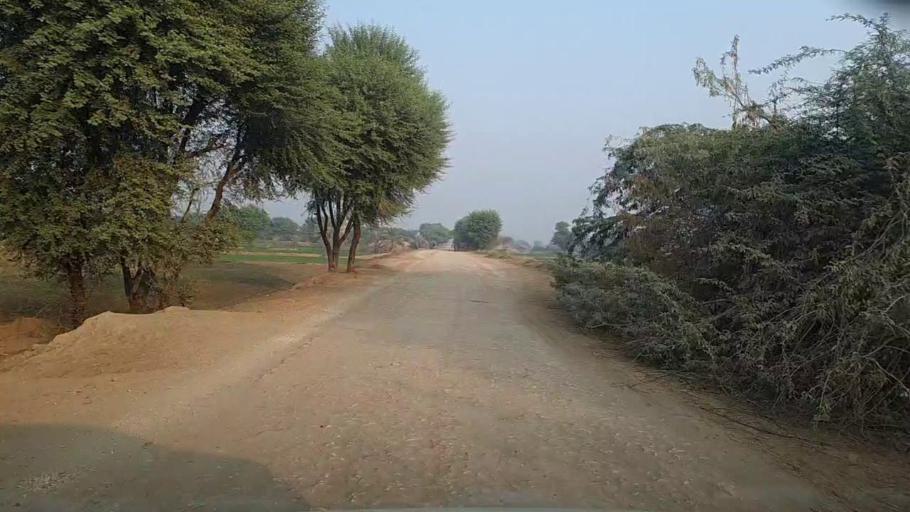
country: PK
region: Sindh
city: Bozdar
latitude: 27.0826
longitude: 68.5440
